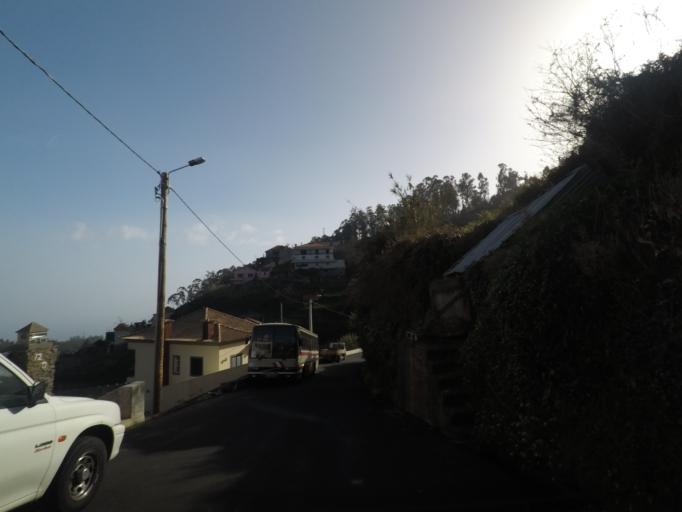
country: PT
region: Madeira
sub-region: Ribeira Brava
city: Campanario
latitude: 32.6793
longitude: -17.0073
